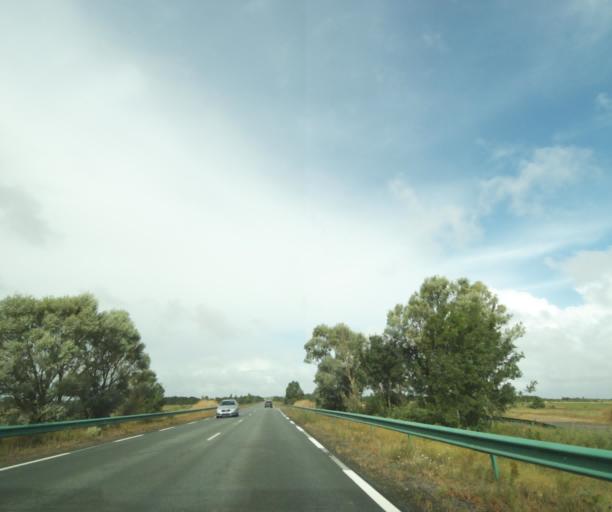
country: FR
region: Poitou-Charentes
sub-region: Departement de la Charente-Maritime
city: Esnandes
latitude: 46.2420
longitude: -1.0861
